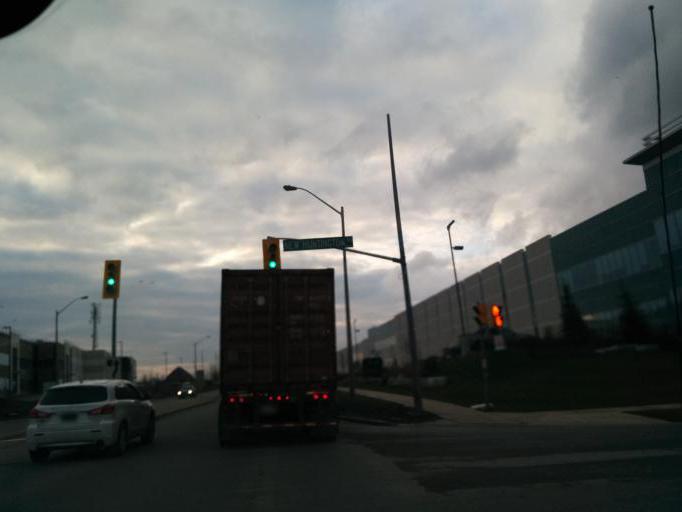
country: CA
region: Ontario
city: Etobicoke
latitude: 43.7752
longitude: -79.6438
